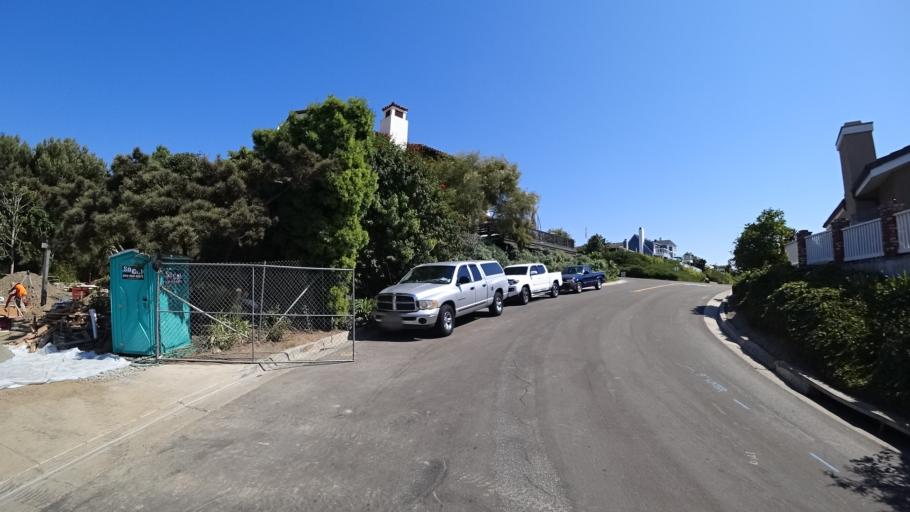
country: US
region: California
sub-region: Orange County
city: San Clemente
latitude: 33.4472
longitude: -117.6414
